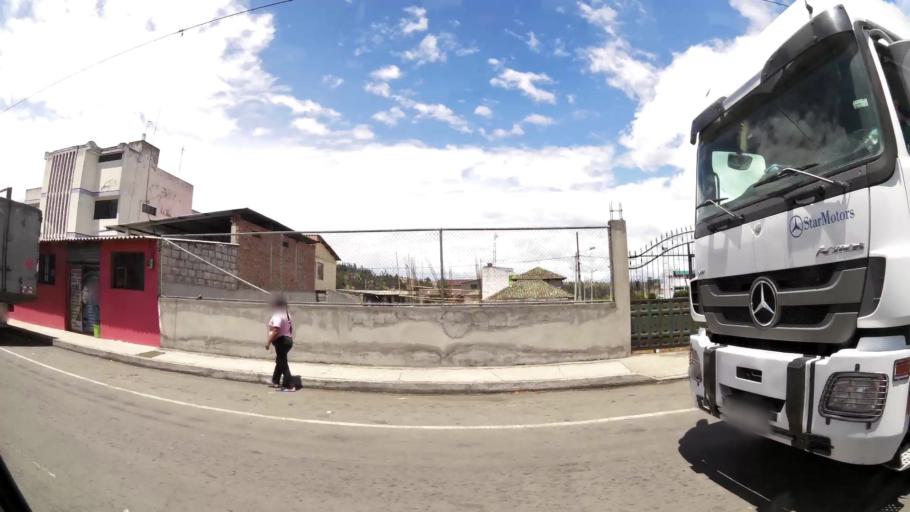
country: EC
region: Tungurahua
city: Pelileo
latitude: -1.3165
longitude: -78.5962
